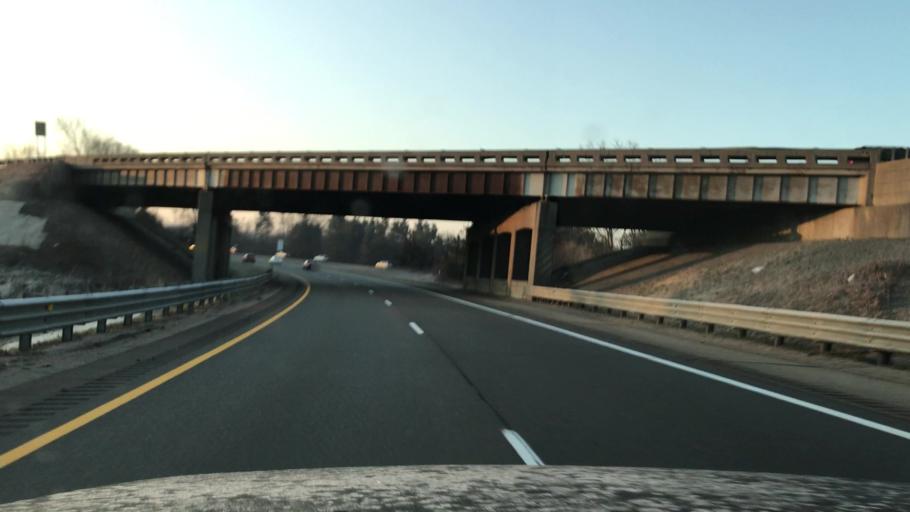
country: US
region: Michigan
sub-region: Kent County
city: East Grand Rapids
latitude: 42.9772
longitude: -85.6041
